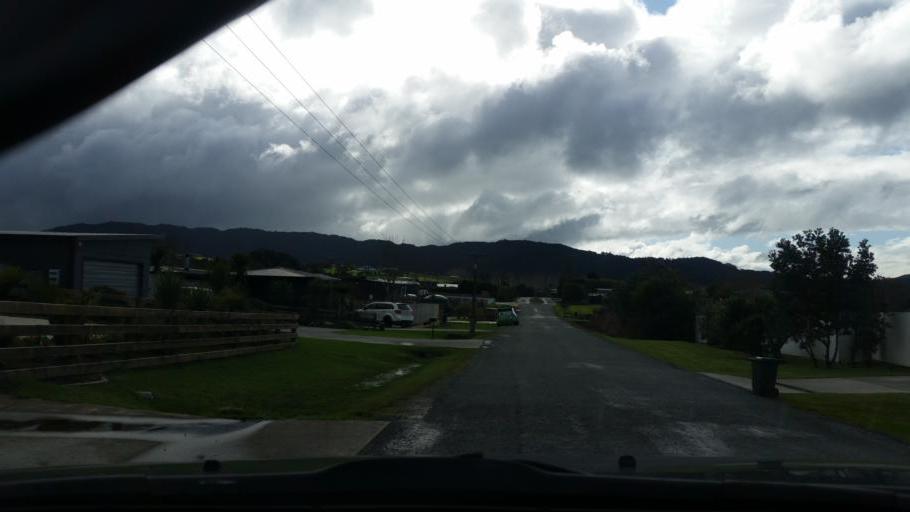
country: NZ
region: Auckland
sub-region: Auckland
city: Wellsford
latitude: -36.0934
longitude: 174.5741
